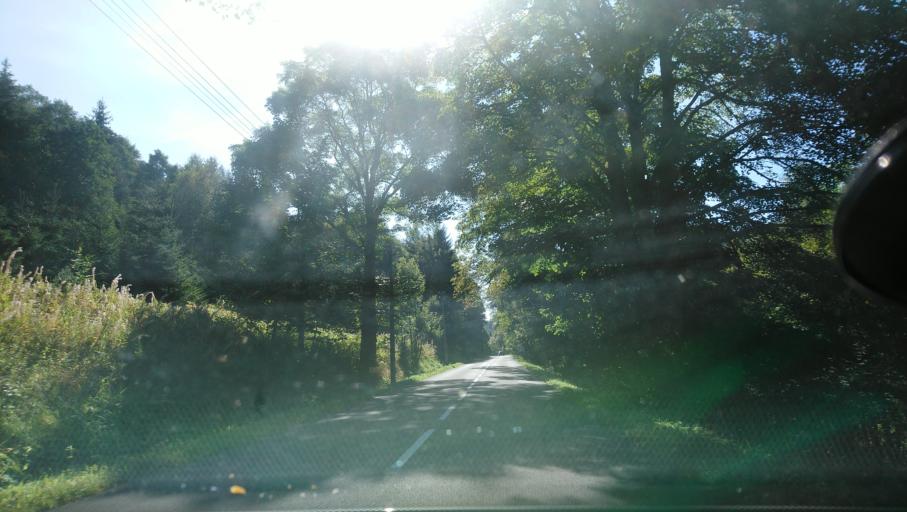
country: CZ
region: Ustecky
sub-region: Okres Chomutov
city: Vejprty
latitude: 50.4622
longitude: 13.0205
